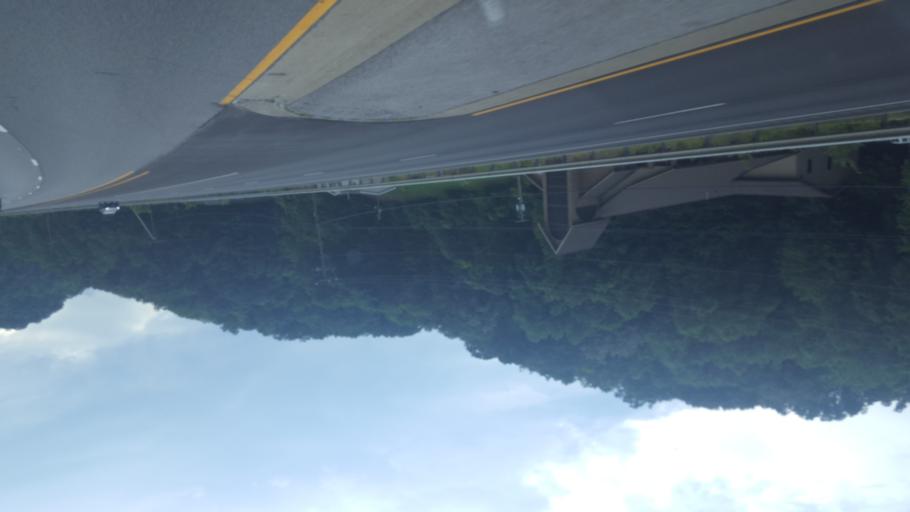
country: US
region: Kentucky
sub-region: Pike County
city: Pikeville
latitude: 37.4165
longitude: -82.5206
